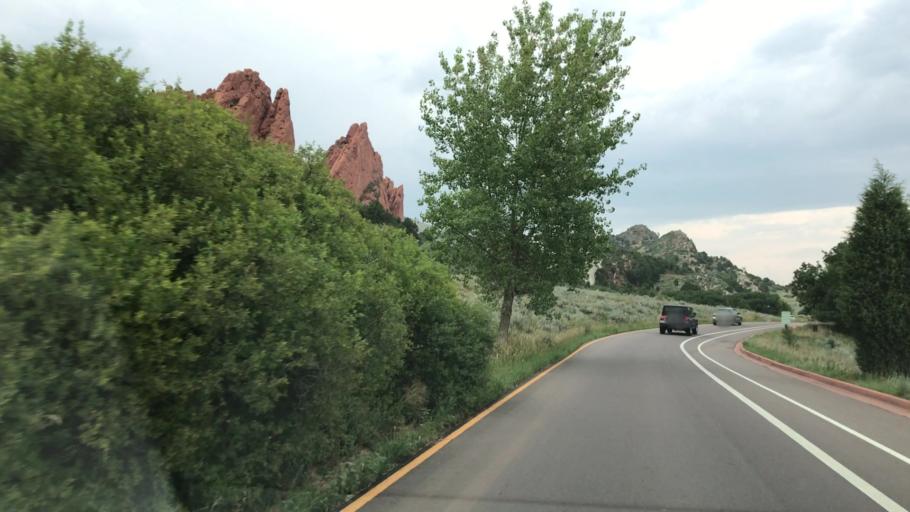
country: US
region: Colorado
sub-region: El Paso County
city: Manitou Springs
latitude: 38.8752
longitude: -104.8783
